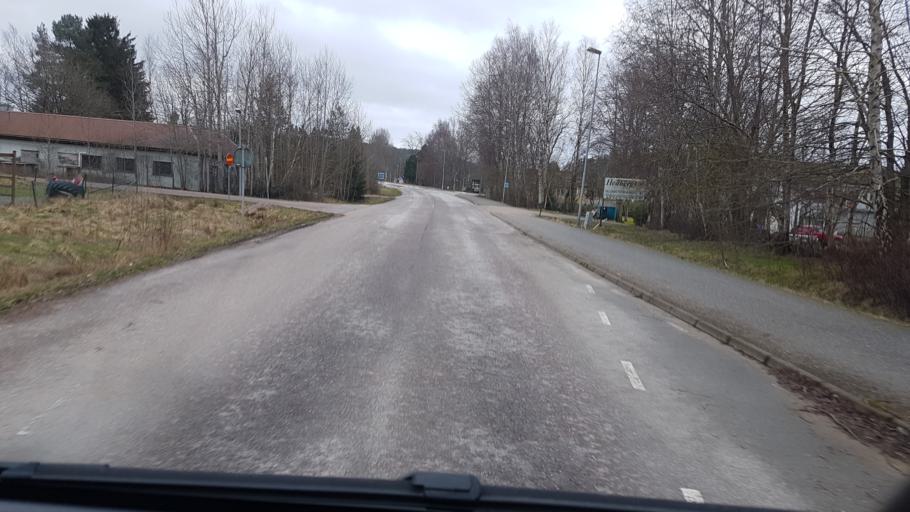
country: SE
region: Vaestra Goetaland
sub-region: Lerums Kommun
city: Stenkullen
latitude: 57.7949
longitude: 12.3080
